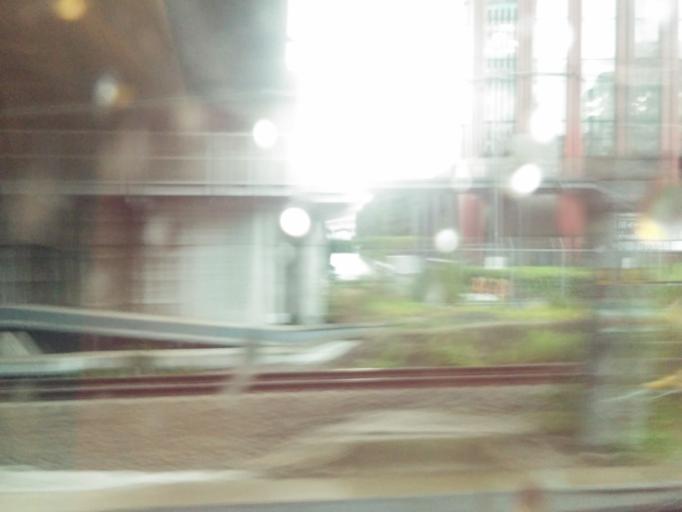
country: JP
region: Tokyo
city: Tokyo
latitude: 35.6435
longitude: 139.7445
